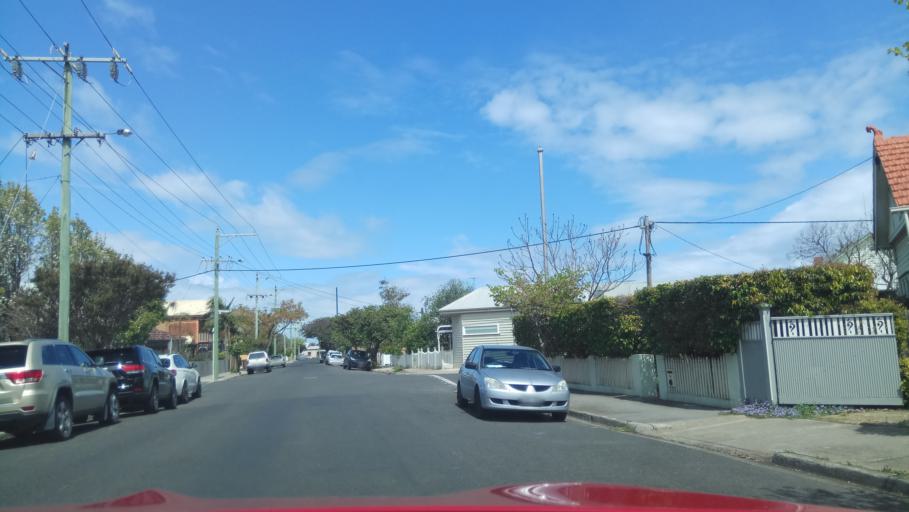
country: AU
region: Victoria
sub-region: Hobsons Bay
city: Williamstown
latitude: -37.8527
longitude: 144.8936
